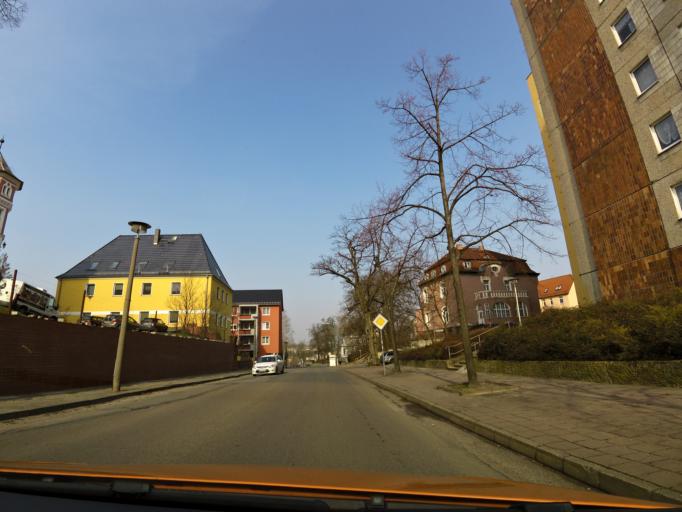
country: DE
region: Brandenburg
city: Frankfurt (Oder)
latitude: 52.3470
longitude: 14.5436
